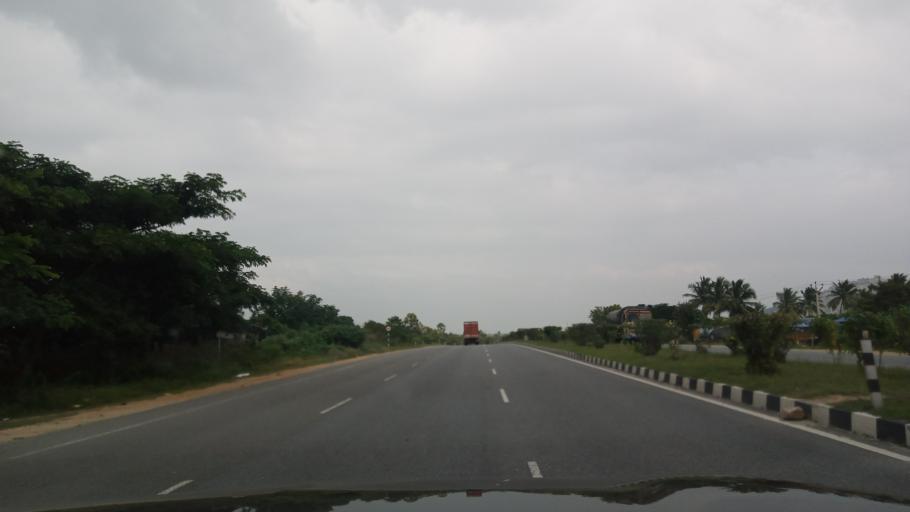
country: IN
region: Tamil Nadu
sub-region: Vellore
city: Jolarpettai
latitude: 12.5551
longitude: 78.4572
